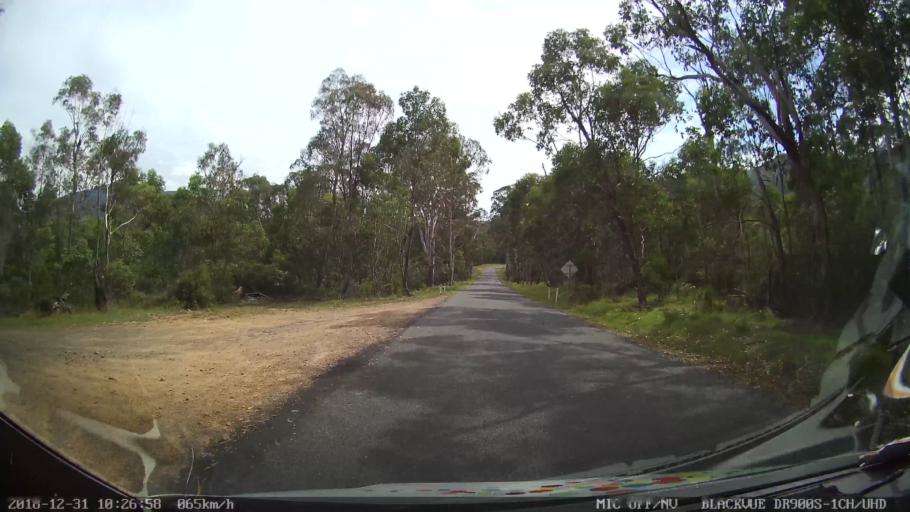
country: AU
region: New South Wales
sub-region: Snowy River
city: Jindabyne
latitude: -36.4901
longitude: 148.1403
